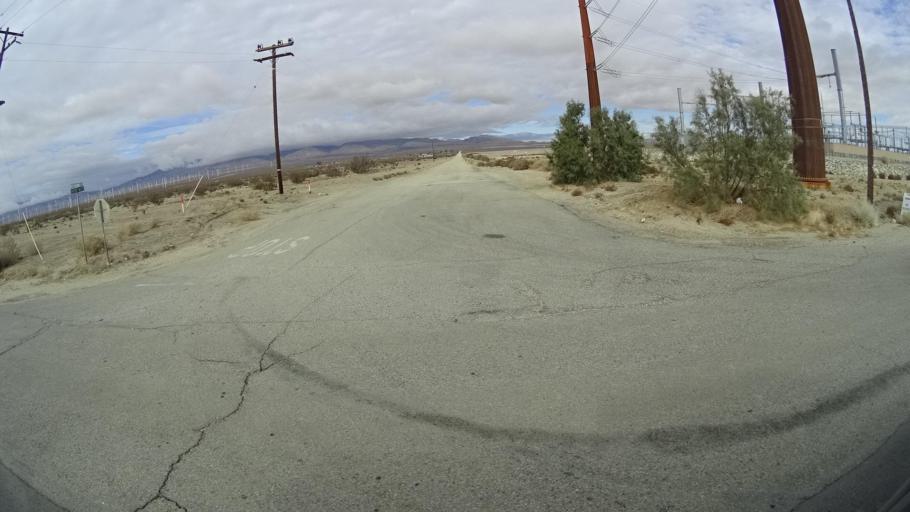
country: US
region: California
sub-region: Kern County
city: Rosamond
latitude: 34.8629
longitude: -118.3797
